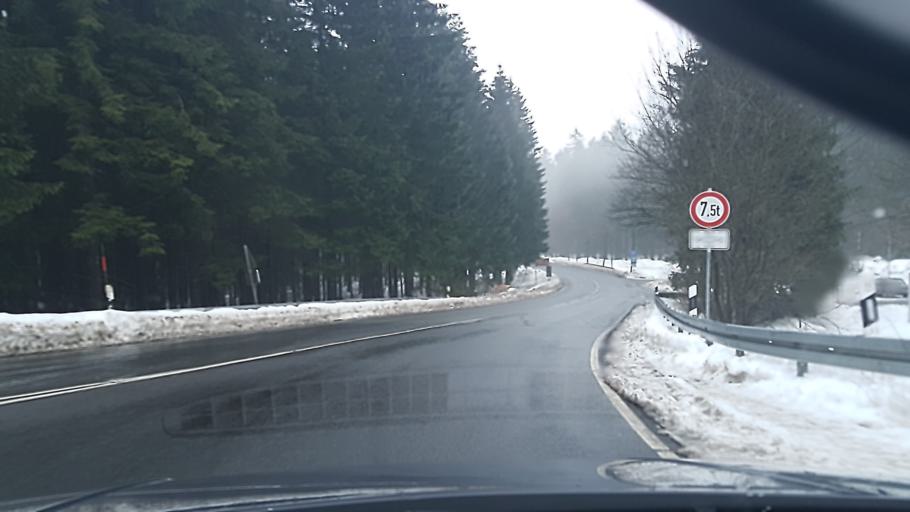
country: DE
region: Lower Saxony
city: Clausthal-Zellerfeld
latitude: 51.8450
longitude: 10.3510
